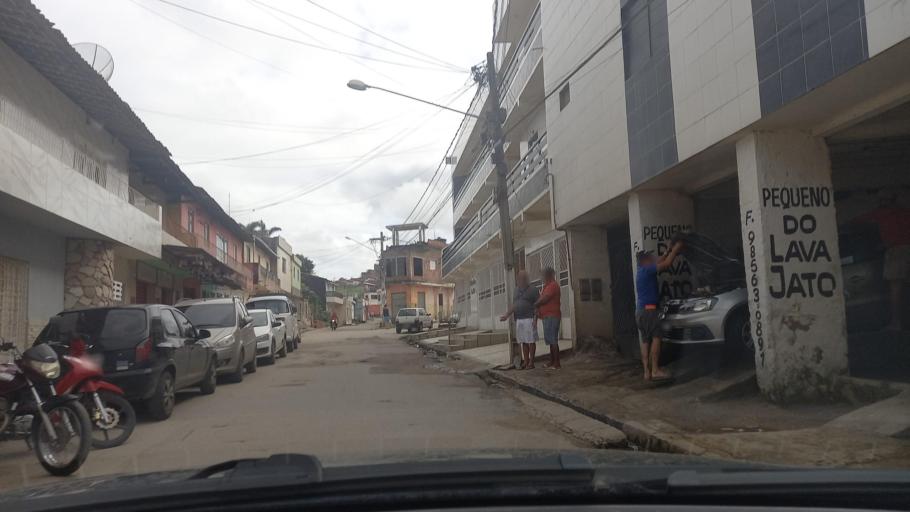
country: BR
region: Pernambuco
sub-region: Vitoria De Santo Antao
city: Vitoria de Santo Antao
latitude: -8.1127
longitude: -35.3007
